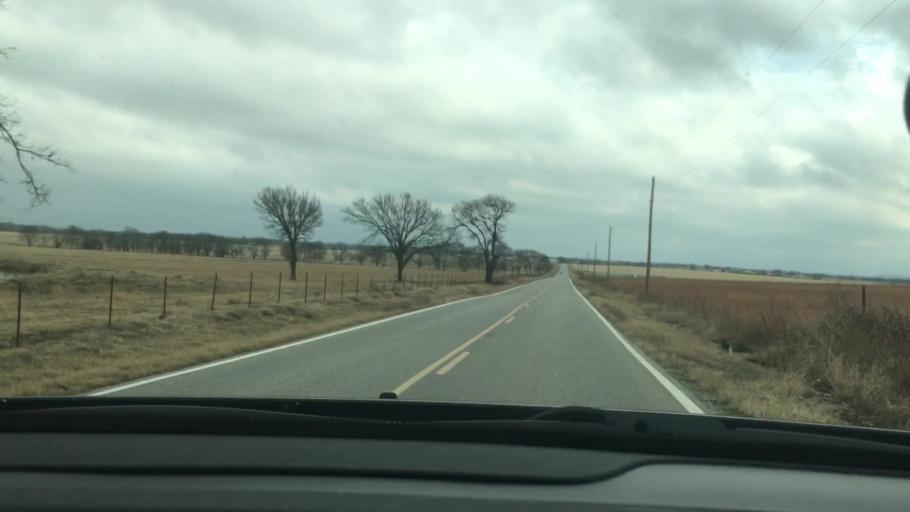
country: US
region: Oklahoma
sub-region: Bryan County
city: Durant
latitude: 34.0887
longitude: -96.4748
